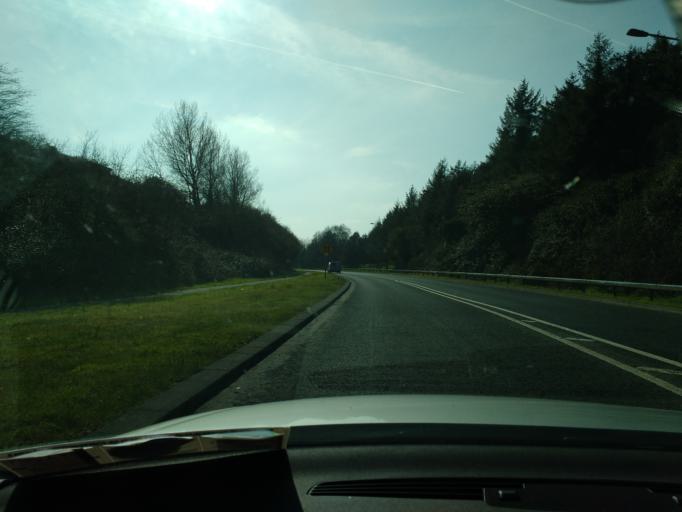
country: IE
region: Munster
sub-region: An Clar
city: Shannon
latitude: 52.7008
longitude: -8.8981
